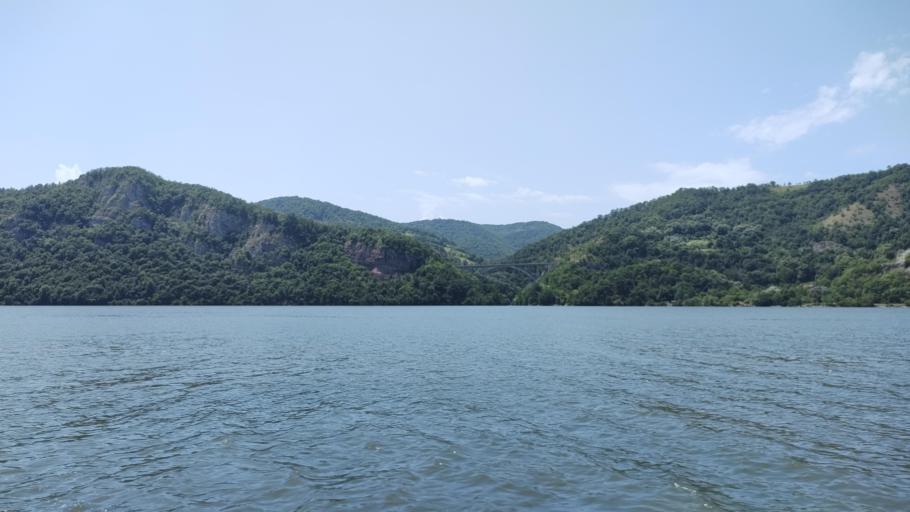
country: RO
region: Mehedinti
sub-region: Comuna Svinita
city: Svinita
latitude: 44.5477
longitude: 22.0382
